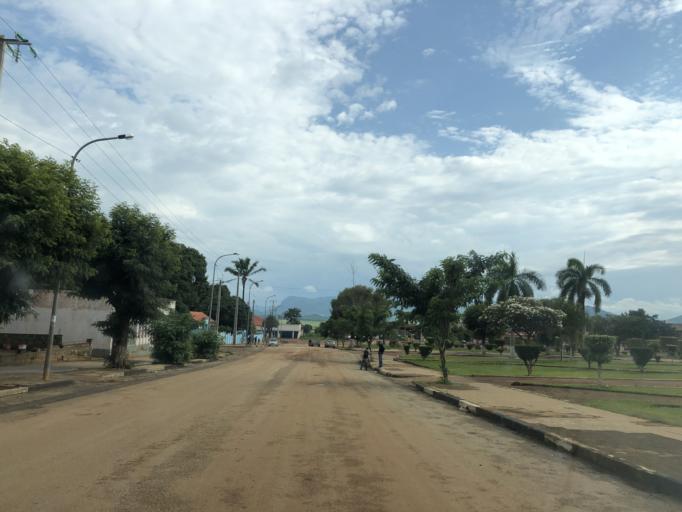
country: AO
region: Cuanza Sul
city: Uacu Cungo
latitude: -11.3634
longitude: 15.1181
